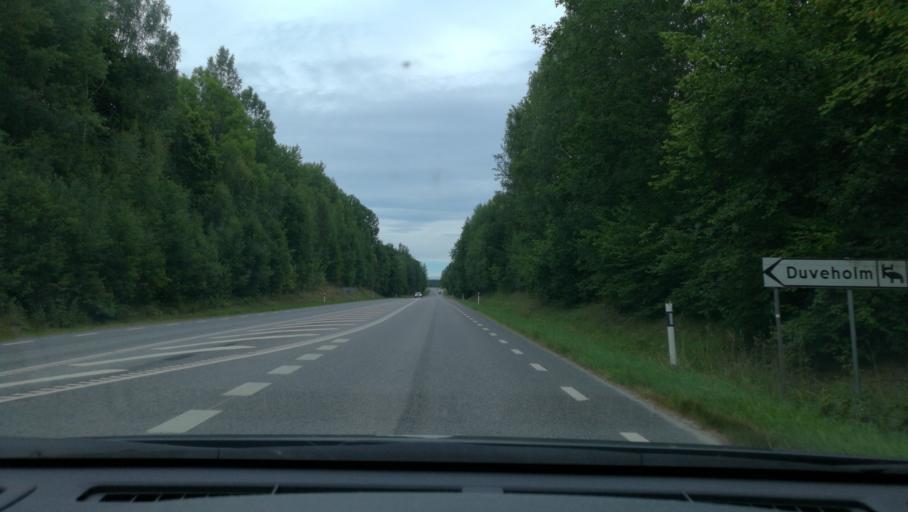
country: SE
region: Soedermanland
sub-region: Katrineholms Kommun
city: Katrineholm
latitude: 58.9704
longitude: 16.2011
